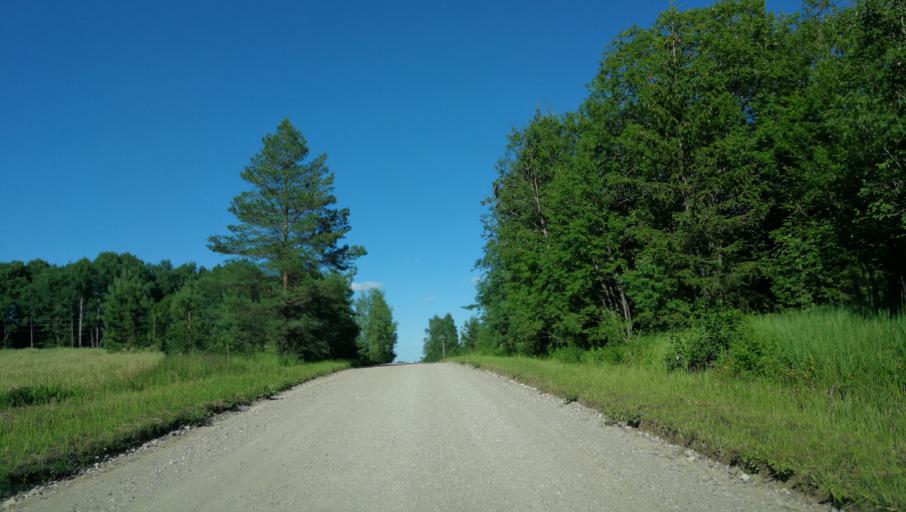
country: LV
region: Jaunpiebalga
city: Jaunpiebalga
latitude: 56.9952
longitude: 26.0221
